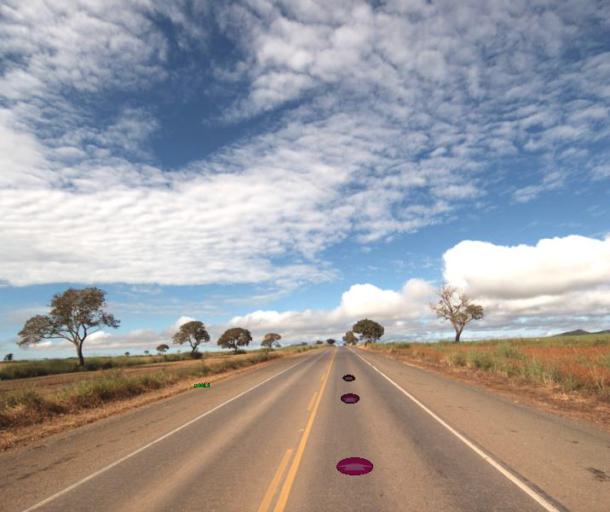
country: BR
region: Goias
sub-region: Uruacu
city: Uruacu
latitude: -14.7036
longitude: -49.2208
